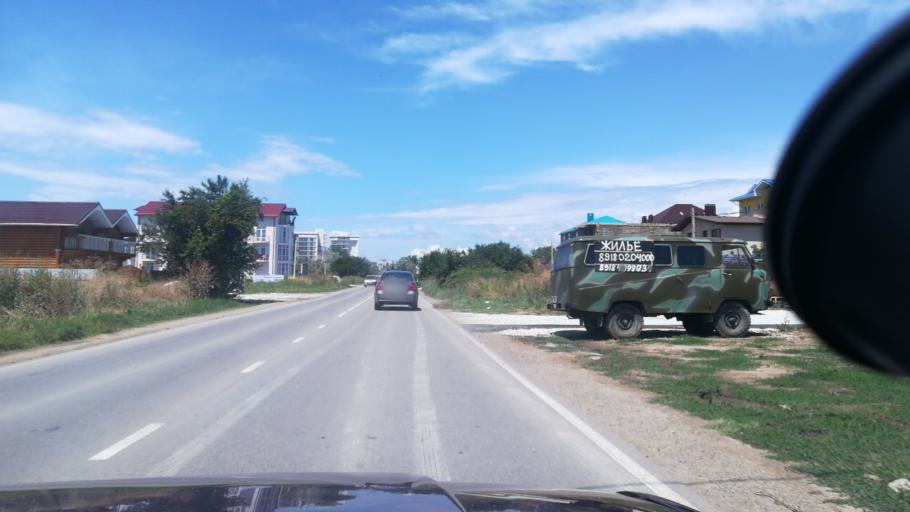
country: RU
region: Krasnodarskiy
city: Vityazevo
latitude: 44.9625
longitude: 37.2924
